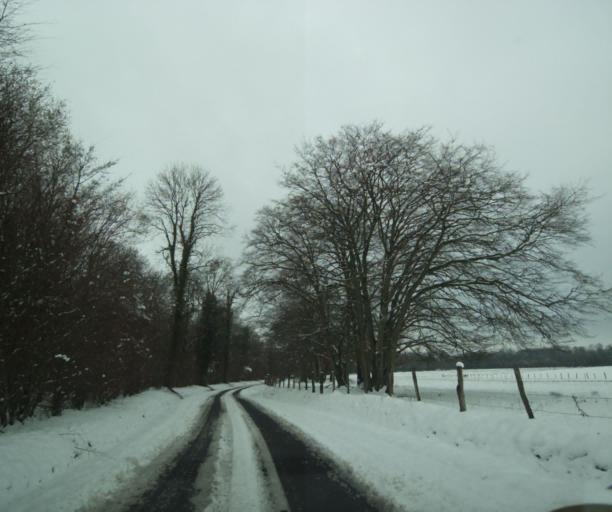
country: FR
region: Champagne-Ardenne
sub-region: Departement de la Haute-Marne
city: Montier-en-Der
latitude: 48.4841
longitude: 4.6845
